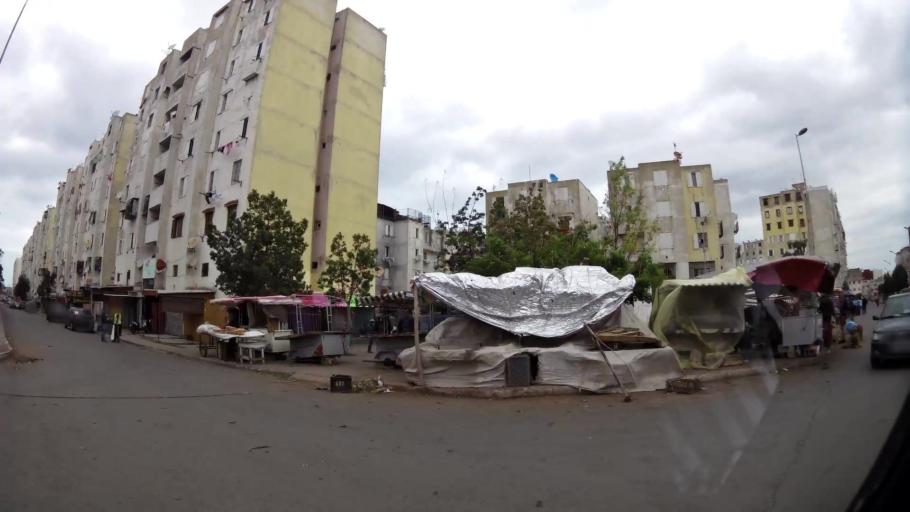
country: MA
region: Grand Casablanca
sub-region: Casablanca
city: Casablanca
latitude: 33.5862
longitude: -7.5533
